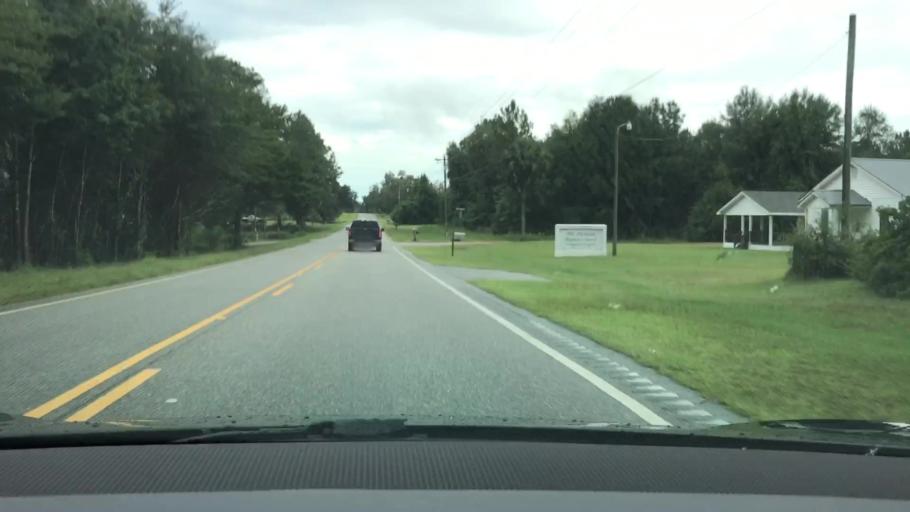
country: US
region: Alabama
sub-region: Geneva County
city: Samson
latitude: 31.0913
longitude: -86.1099
